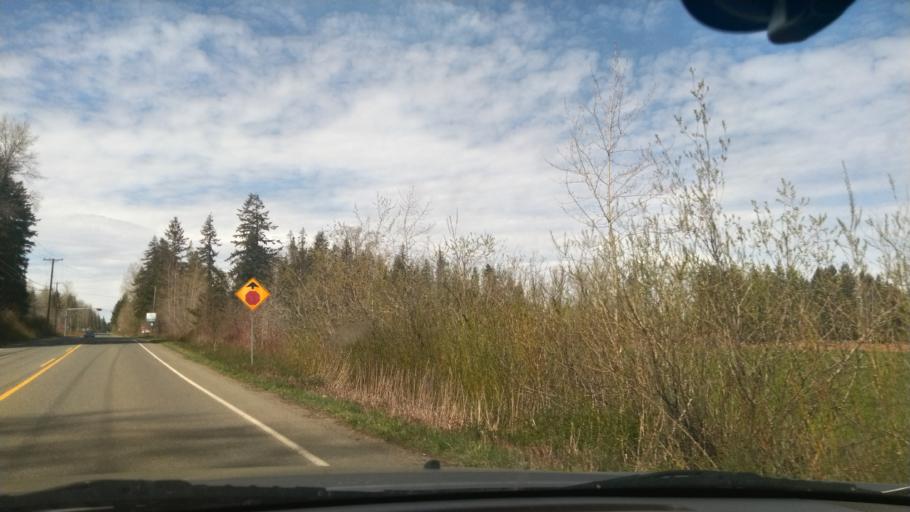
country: CA
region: British Columbia
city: Courtenay
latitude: 49.7051
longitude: -125.0236
